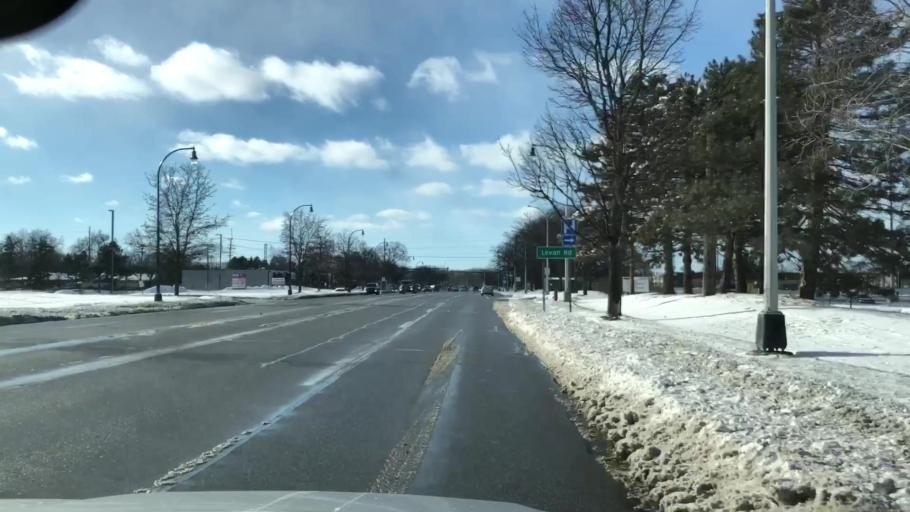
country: US
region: Michigan
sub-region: Wayne County
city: Westland
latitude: 42.3679
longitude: -83.3986
